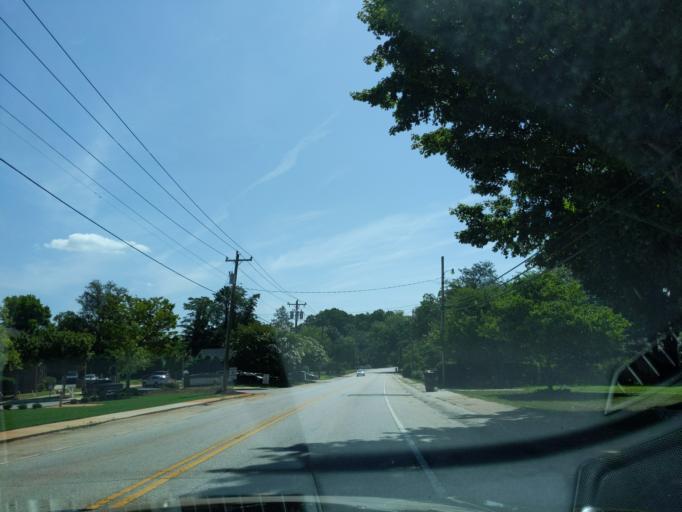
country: US
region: South Carolina
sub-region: Greenville County
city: Taylors
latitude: 34.9195
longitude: -82.3090
